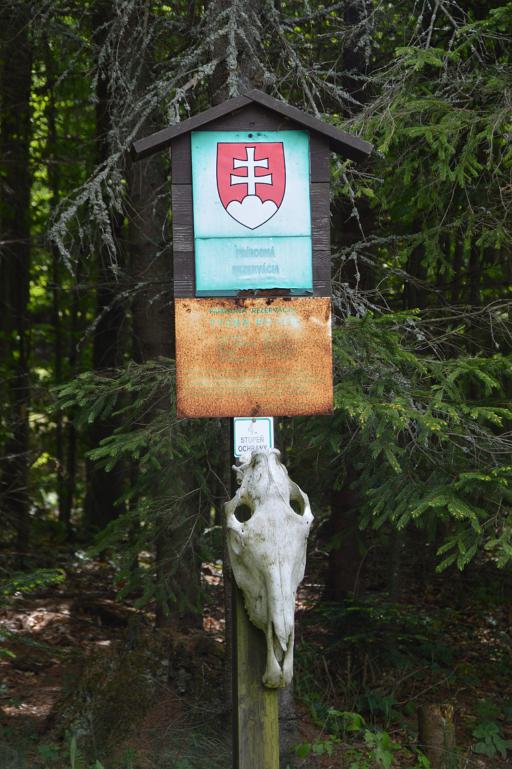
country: SK
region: Kosicky
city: Dobsina
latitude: 48.9068
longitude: 20.3597
